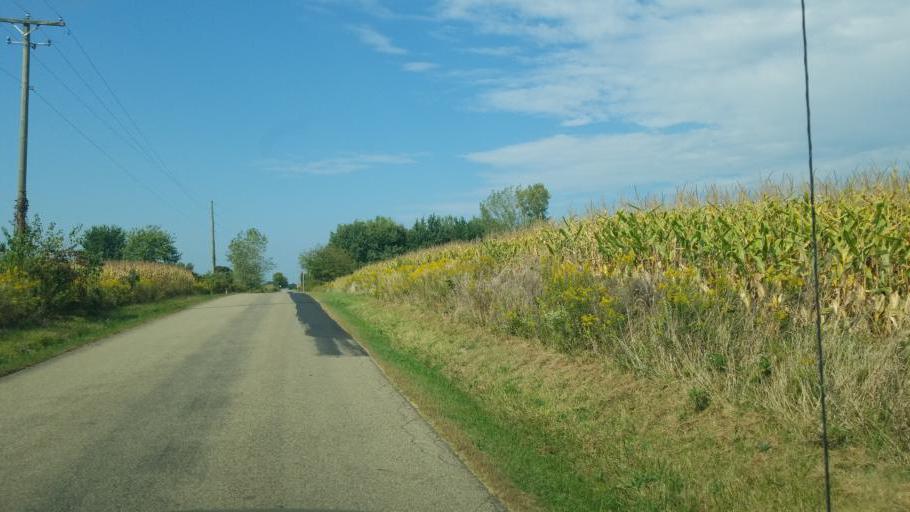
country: US
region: Ohio
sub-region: Knox County
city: Mount Vernon
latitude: 40.3475
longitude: -82.4959
